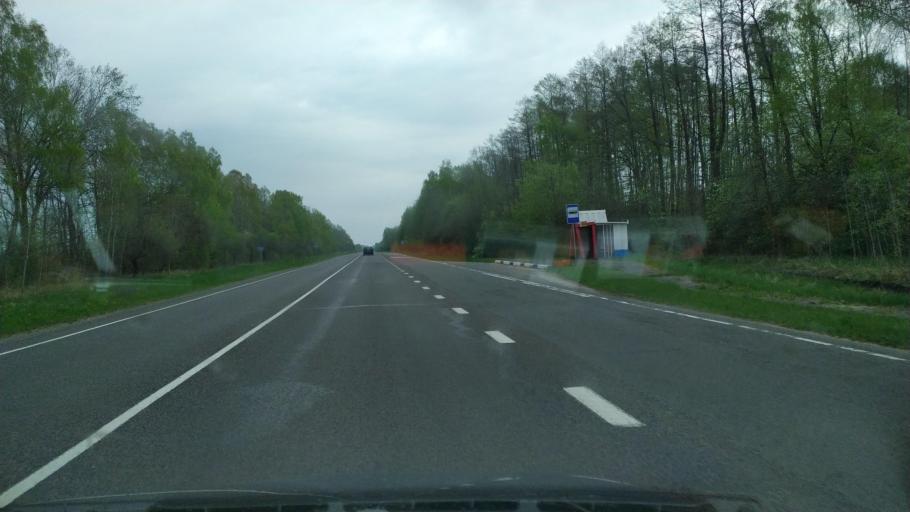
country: BY
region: Brest
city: Horad Kobryn
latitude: 52.3123
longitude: 24.5432
